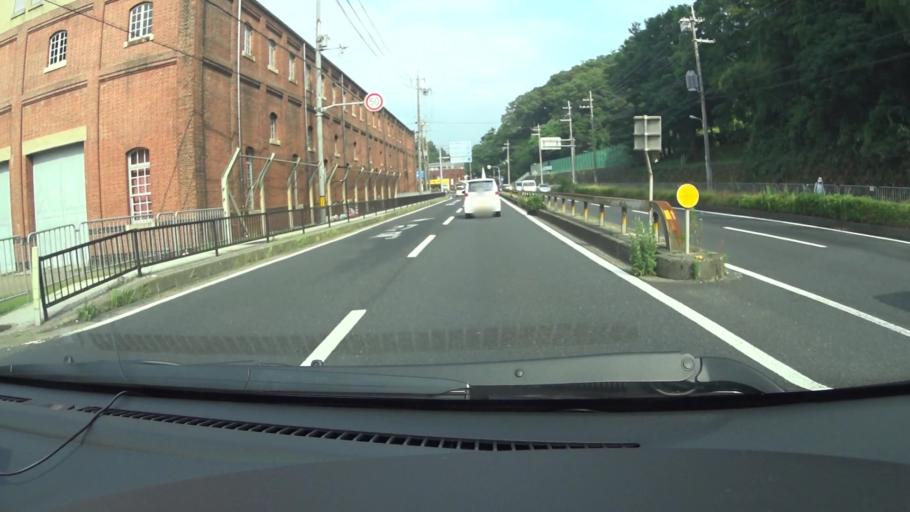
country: JP
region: Kyoto
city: Kameoka
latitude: 35.0630
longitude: 135.5291
